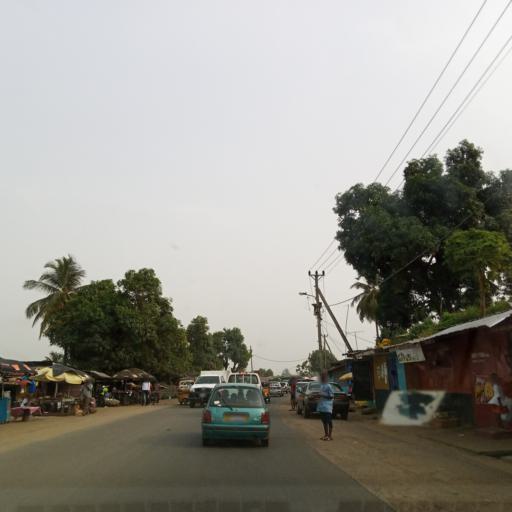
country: LR
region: Montserrado
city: Monrovia
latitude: 6.3031
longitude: -10.7939
